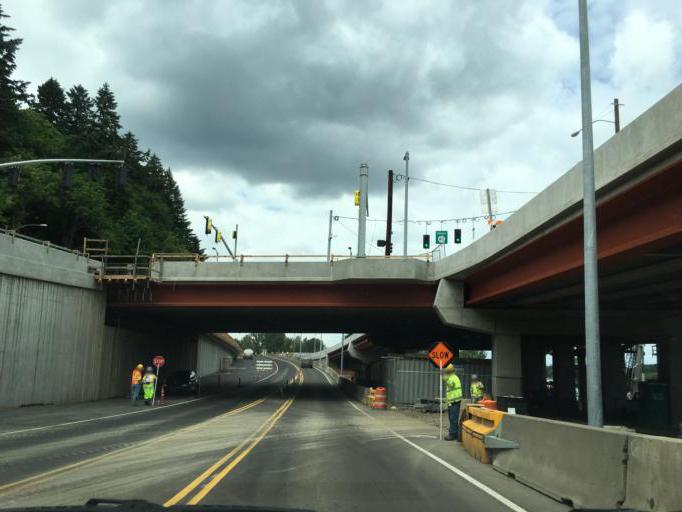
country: US
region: Oregon
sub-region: Clackamas County
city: Milwaukie
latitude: 45.4638
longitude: -122.6688
